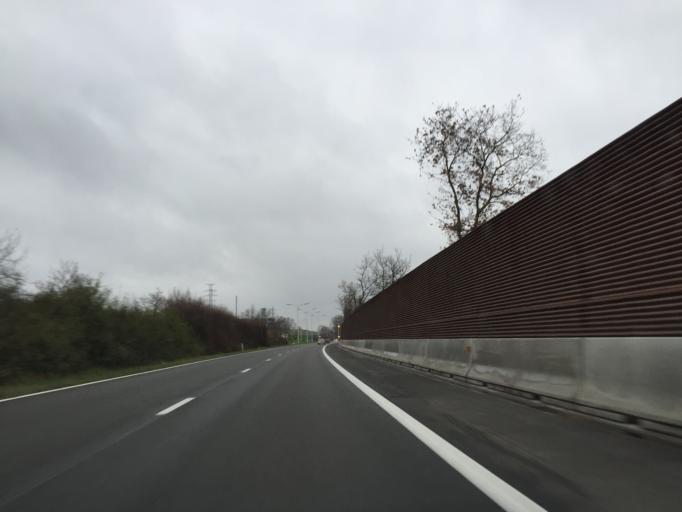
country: BE
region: Flanders
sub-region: Provincie Oost-Vlaanderen
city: Evergem
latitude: 51.1137
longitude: 3.7280
